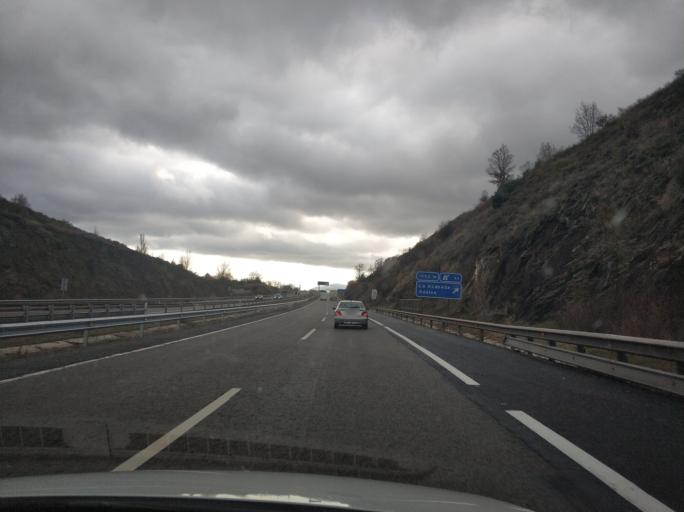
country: ES
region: Madrid
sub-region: Provincia de Madrid
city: Horcajo de la Sierra
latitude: 41.0759
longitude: -3.6040
